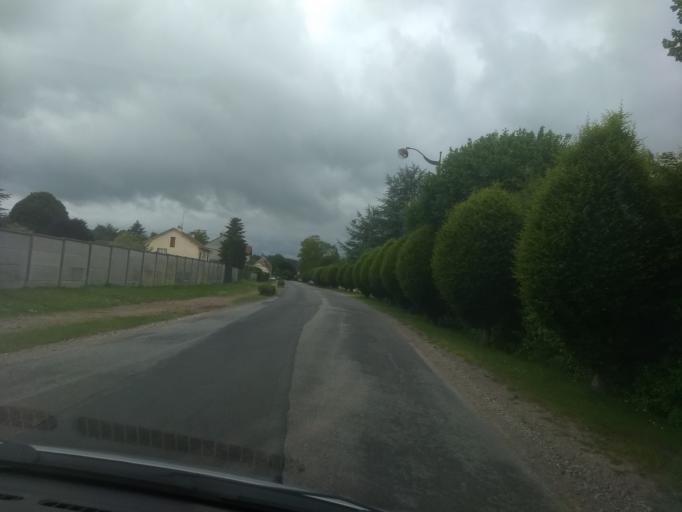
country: FR
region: Lower Normandy
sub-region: Departement de l'Orne
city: Remalard
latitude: 48.4261
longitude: 0.7638
